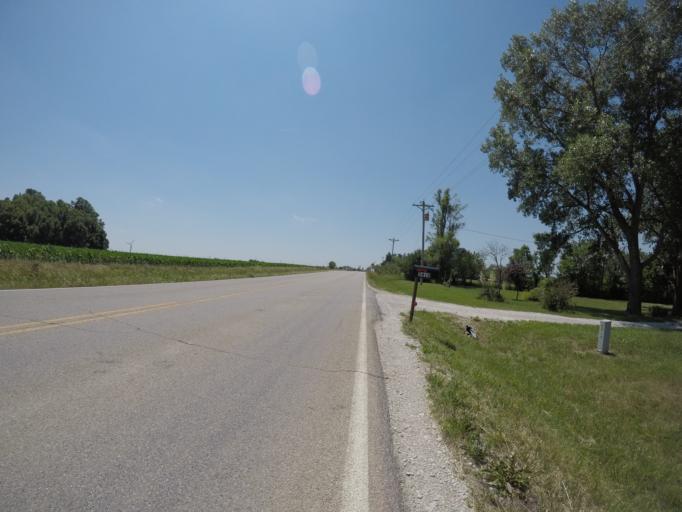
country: US
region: Kansas
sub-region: Riley County
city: Manhattan
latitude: 39.2367
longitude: -96.4454
